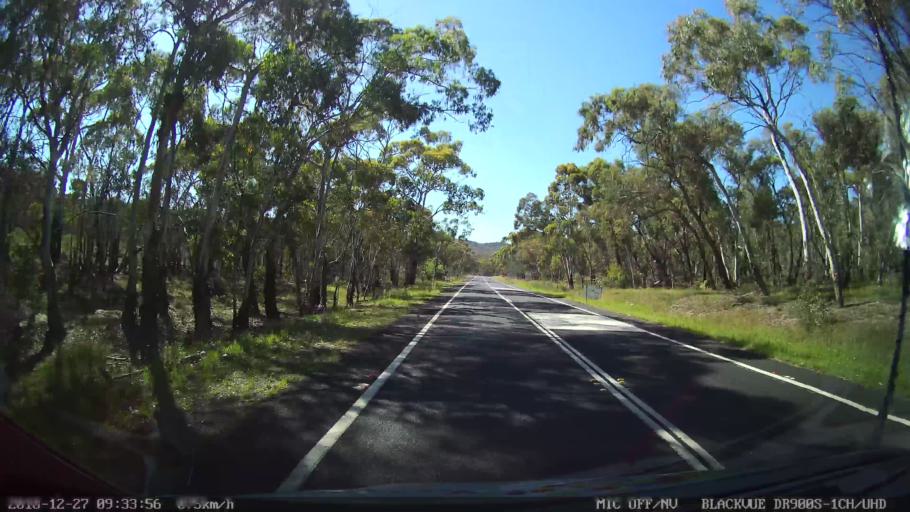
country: AU
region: New South Wales
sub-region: Lithgow
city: Portland
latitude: -33.2207
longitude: 150.0245
